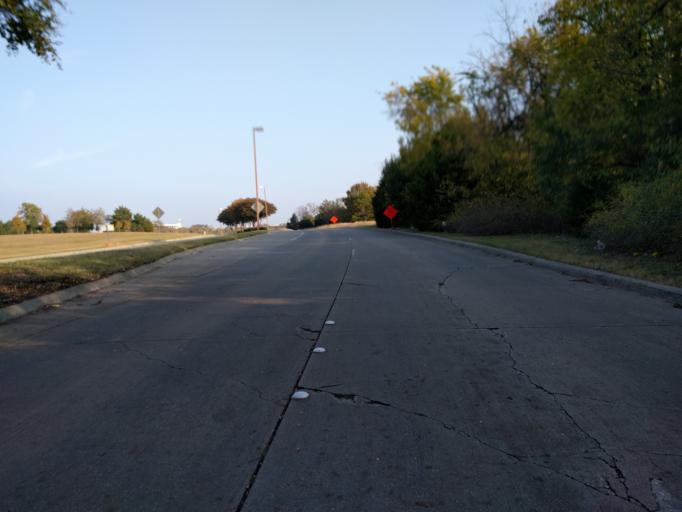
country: US
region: Texas
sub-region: Collin County
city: Plano
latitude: 32.9871
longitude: -96.7038
